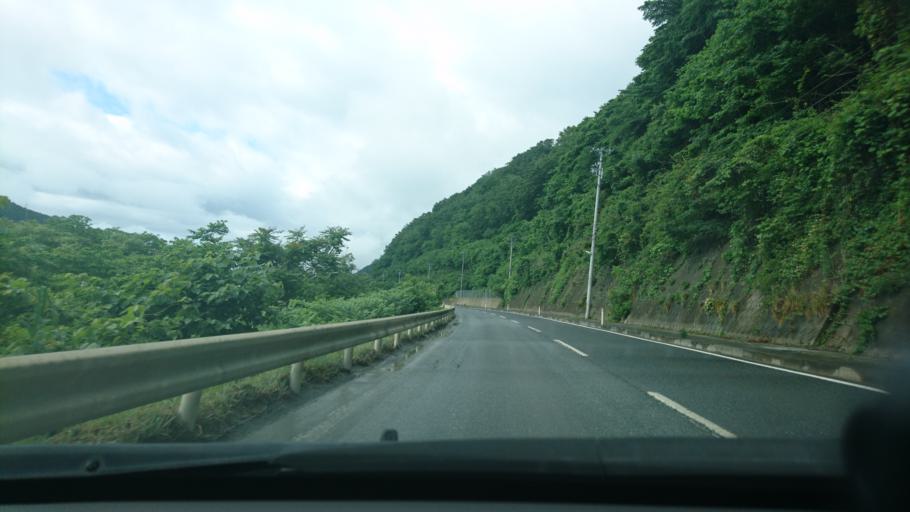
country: JP
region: Miyagi
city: Ishinomaki
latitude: 38.5830
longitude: 141.3039
